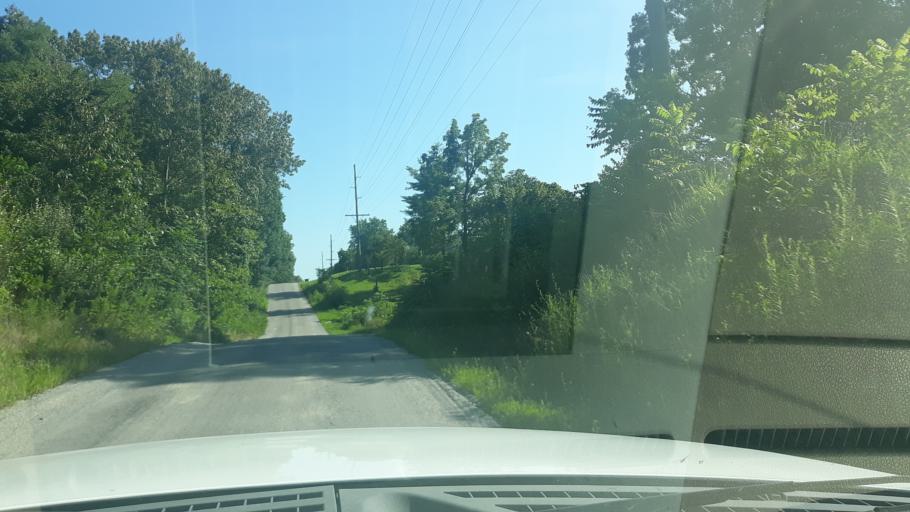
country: US
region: Illinois
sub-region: Saline County
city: Harrisburg
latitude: 37.8541
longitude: -88.5963
